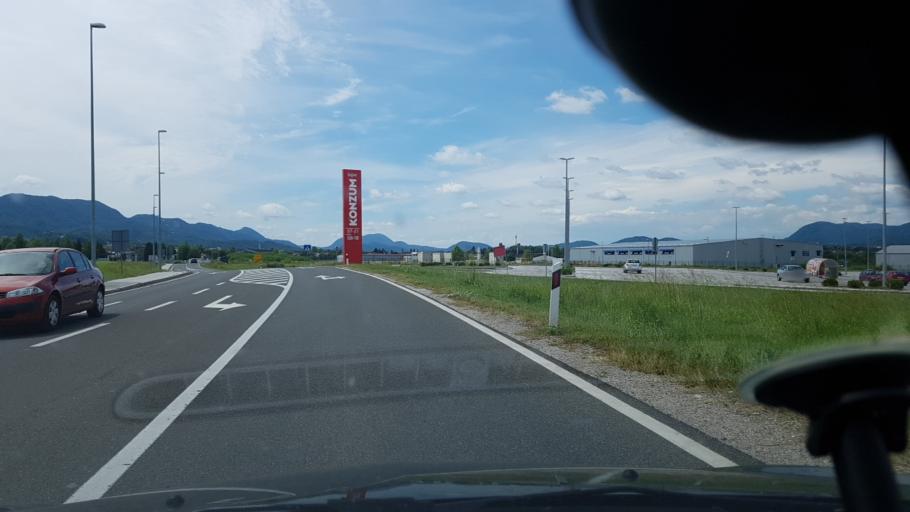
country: HR
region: Varazdinska
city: Ivanec
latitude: 46.2326
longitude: 16.1430
